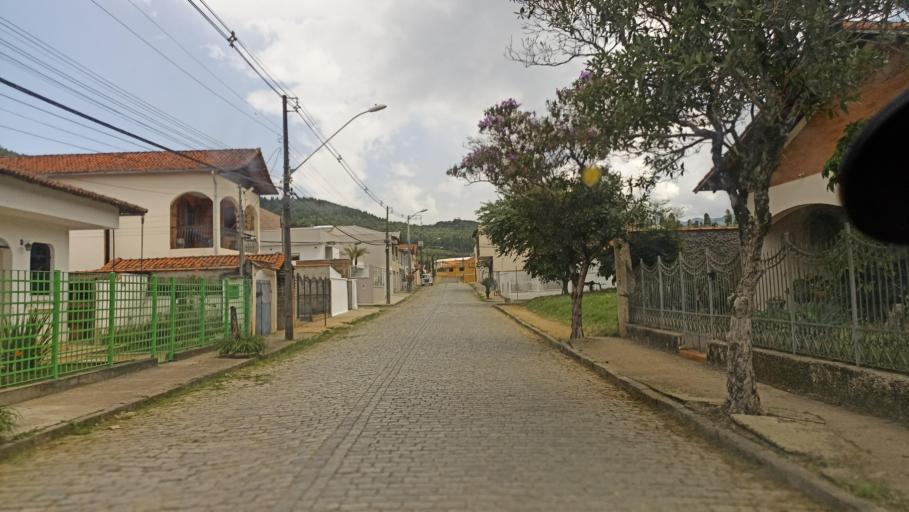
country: BR
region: Minas Gerais
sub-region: Passa Quatro
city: Passa Quatro
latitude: -22.3939
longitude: -44.9650
